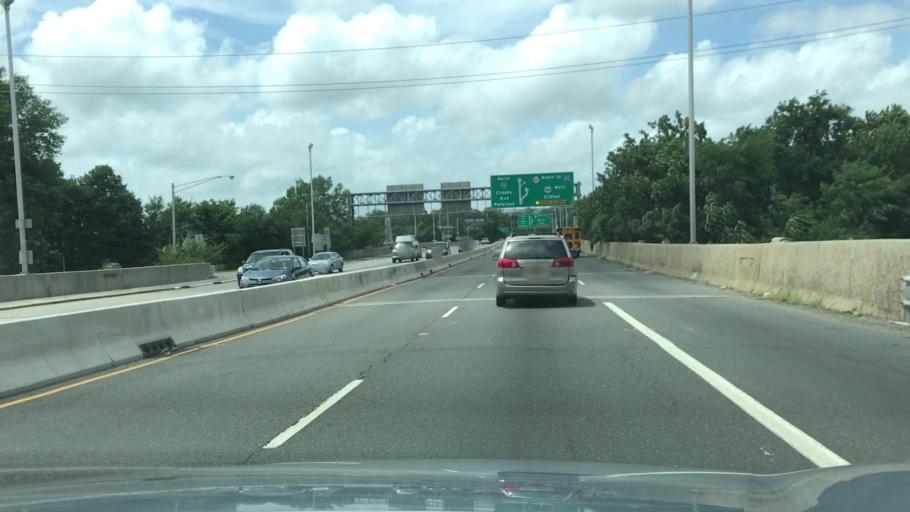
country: US
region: New Jersey
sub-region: Bergen County
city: Elmwood Park
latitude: 40.8937
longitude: -74.1264
